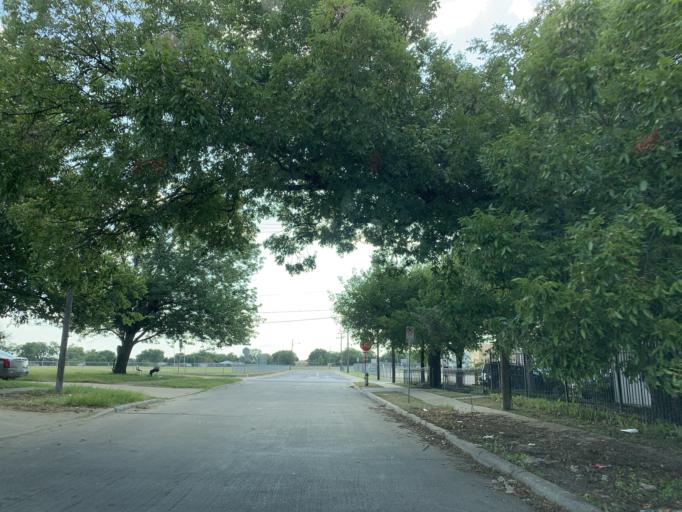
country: US
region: Texas
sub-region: Dallas County
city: Hutchins
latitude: 32.6934
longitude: -96.7816
